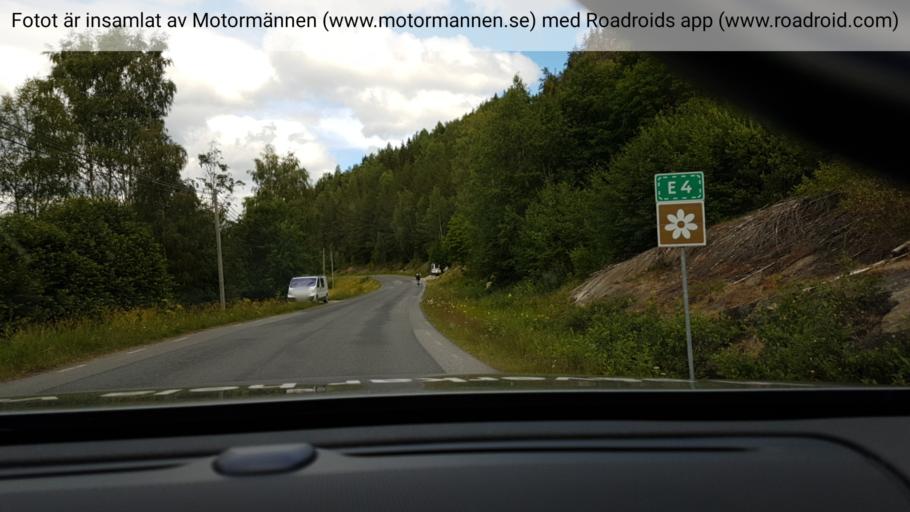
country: SE
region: Vaesternorrland
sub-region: Kramfors Kommun
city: Nordingra
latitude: 62.9139
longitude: 18.2989
